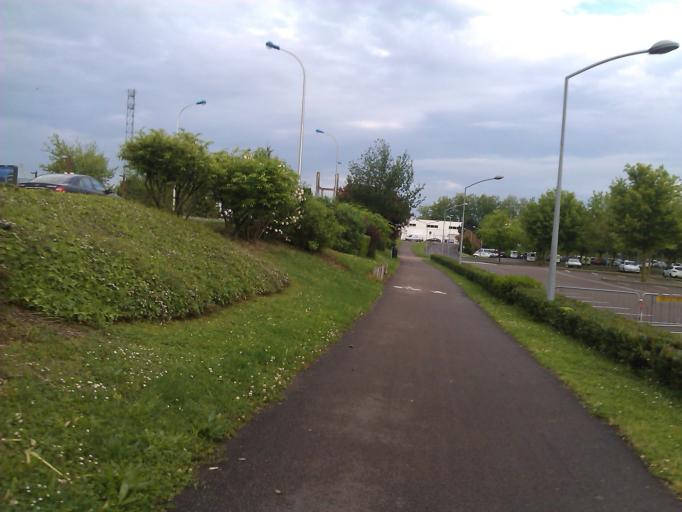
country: FR
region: Bourgogne
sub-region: Departement de Saone-et-Loire
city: Chalon-sur-Saone
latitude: 46.7876
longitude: 4.8656
